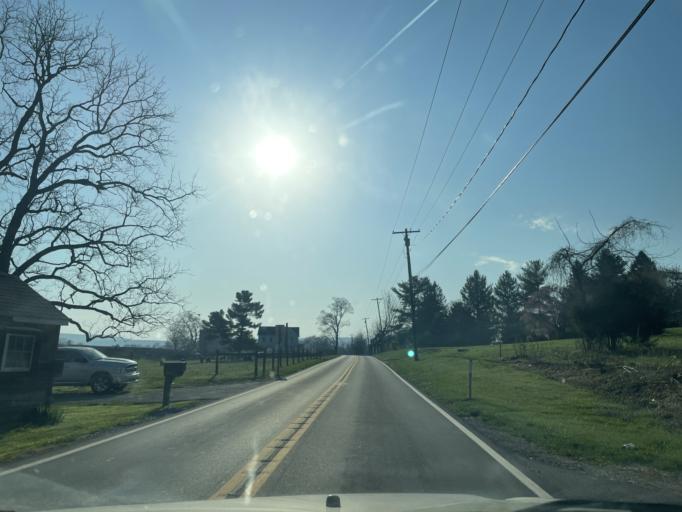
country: US
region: Maryland
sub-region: Washington County
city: Keedysville
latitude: 39.5330
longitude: -77.7022
